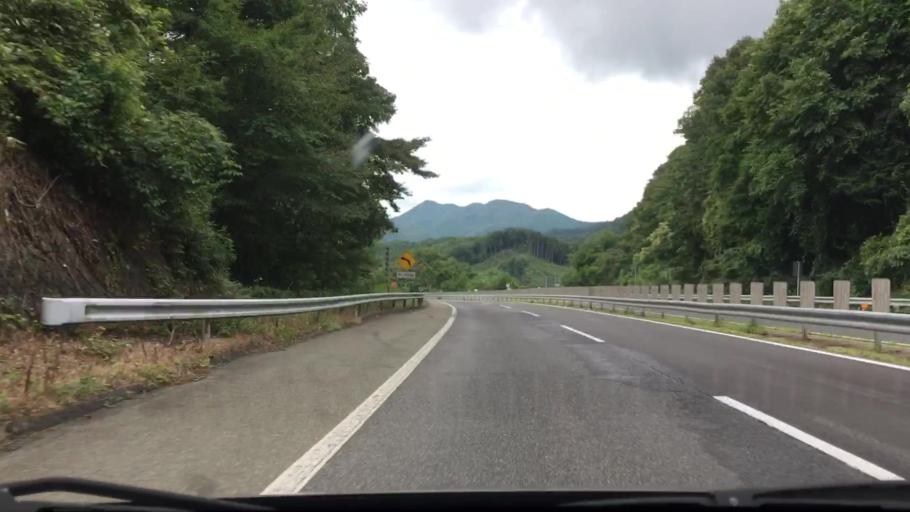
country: JP
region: Okayama
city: Niimi
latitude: 34.8912
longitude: 133.2624
